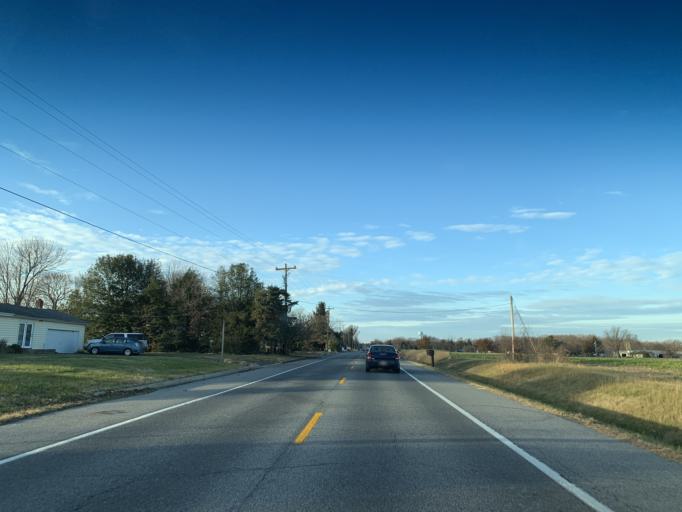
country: US
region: Maryland
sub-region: Kent County
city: Chestertown
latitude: 39.2659
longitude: -76.0880
